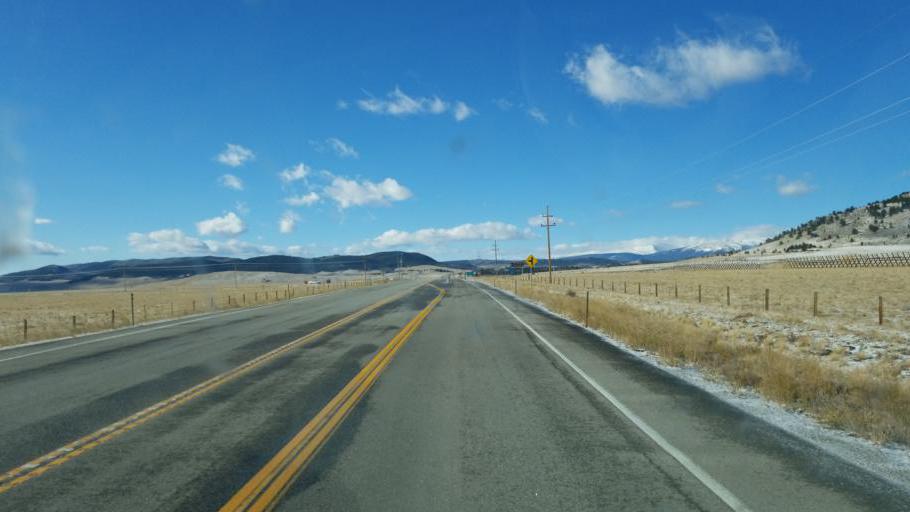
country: US
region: Colorado
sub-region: Park County
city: Fairplay
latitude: 39.3179
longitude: -105.8804
